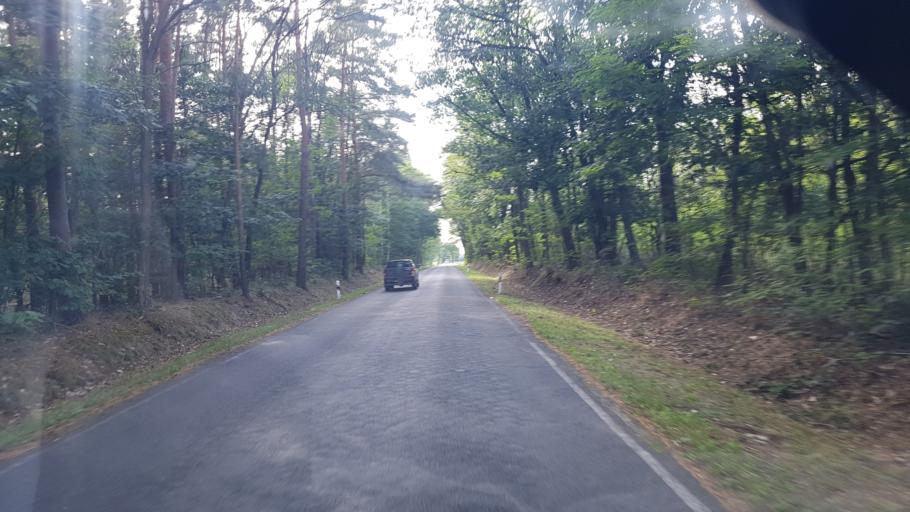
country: DE
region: Brandenburg
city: Welzow
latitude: 51.5561
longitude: 14.1573
